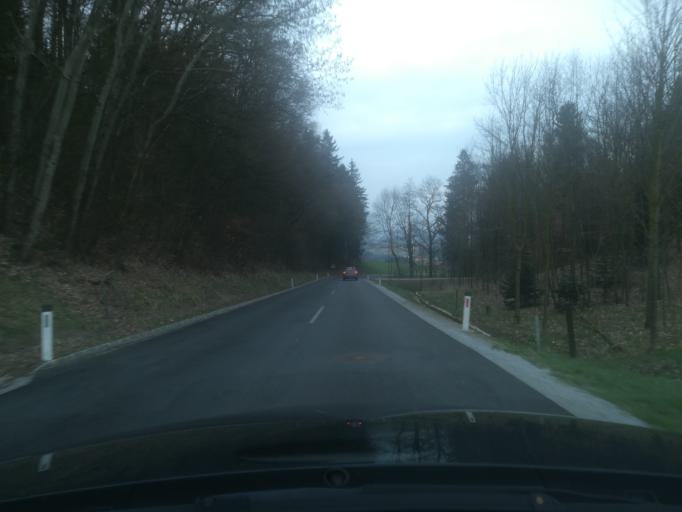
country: AT
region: Upper Austria
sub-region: Politischer Bezirk Urfahr-Umgebung
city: Feldkirchen an der Donau
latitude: 48.3345
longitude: 13.9588
